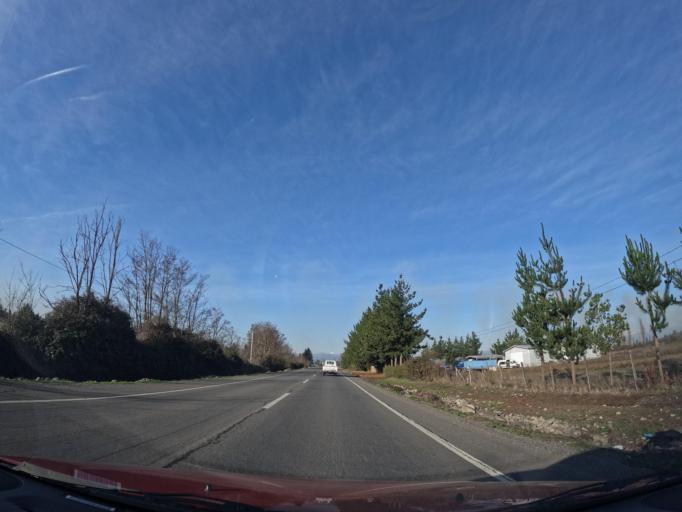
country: CL
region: Maule
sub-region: Provincia de Linares
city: Colbun
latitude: -35.6275
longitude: -71.4661
